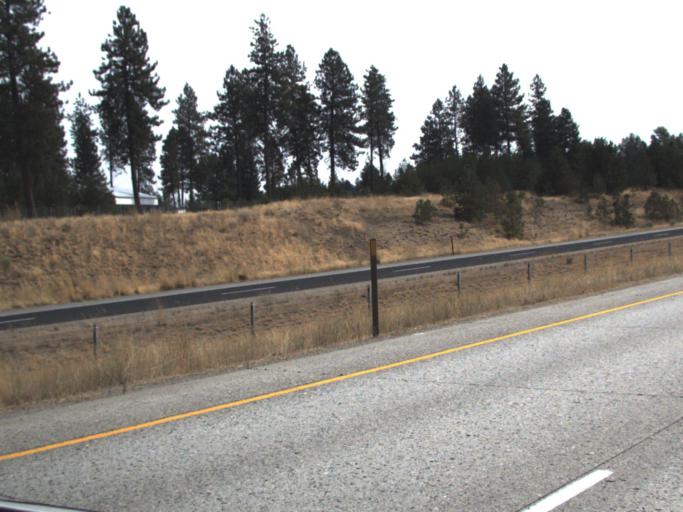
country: US
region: Washington
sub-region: Spokane County
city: Fairwood
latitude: 47.8176
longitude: -117.4109
